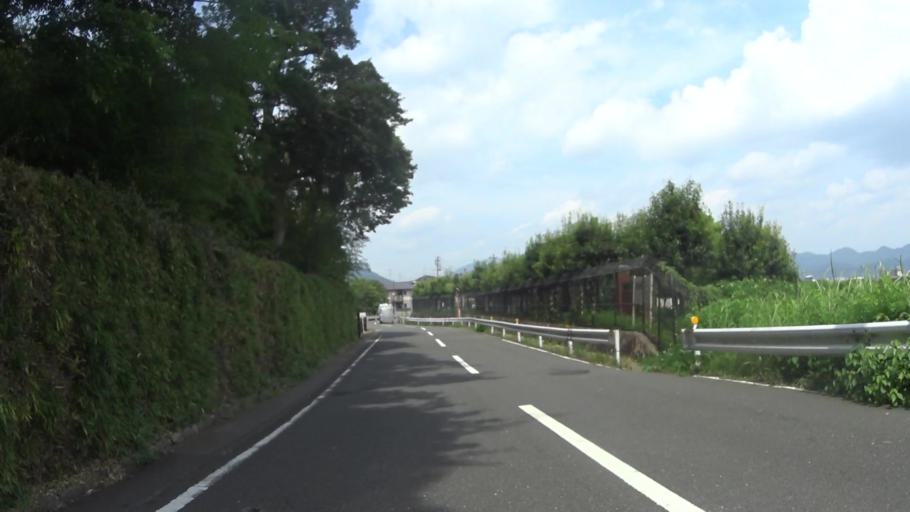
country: JP
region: Kyoto
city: Muko
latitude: 34.9850
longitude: 135.7106
